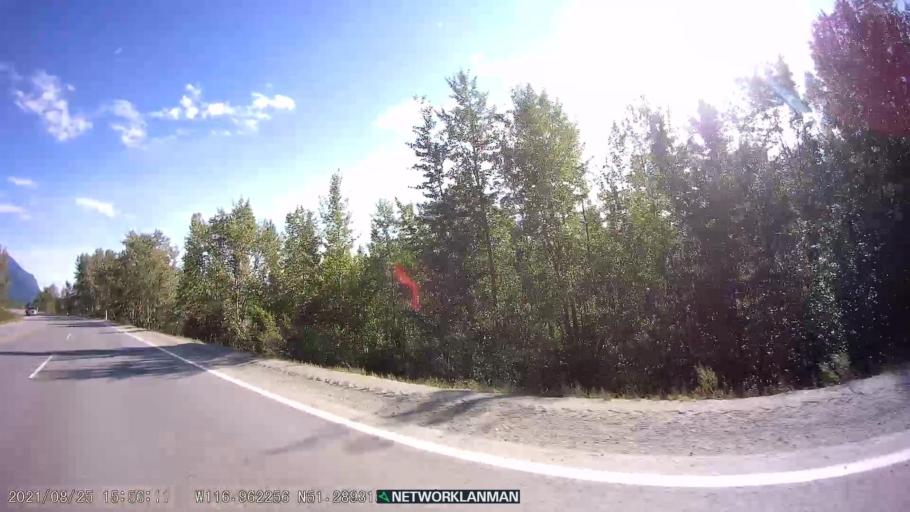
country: CA
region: British Columbia
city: Golden
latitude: 51.2891
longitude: -116.9635
